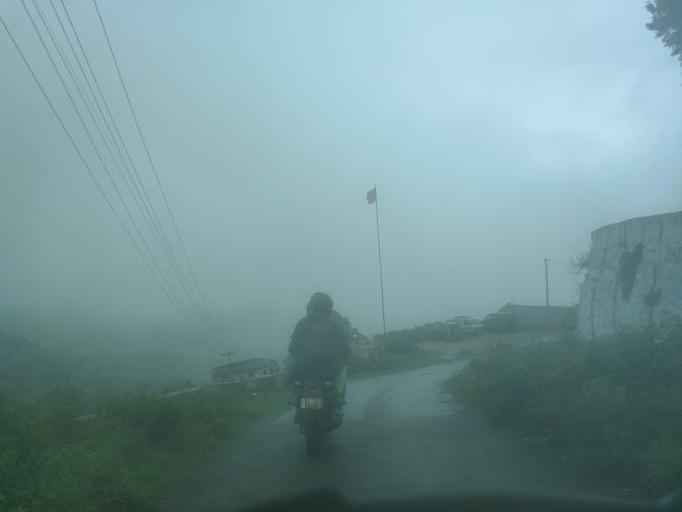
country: IN
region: Tamil Nadu
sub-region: Dindigul
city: Kodaikanal
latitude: 10.2337
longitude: 77.3276
